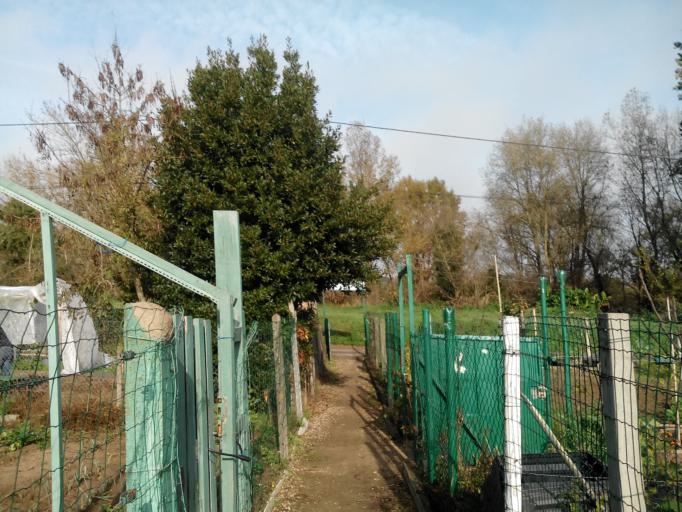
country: FR
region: Centre
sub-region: Departement d'Indre-et-Loire
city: Saint-Cyr-sur-Loire
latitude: 47.3868
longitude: 0.6373
